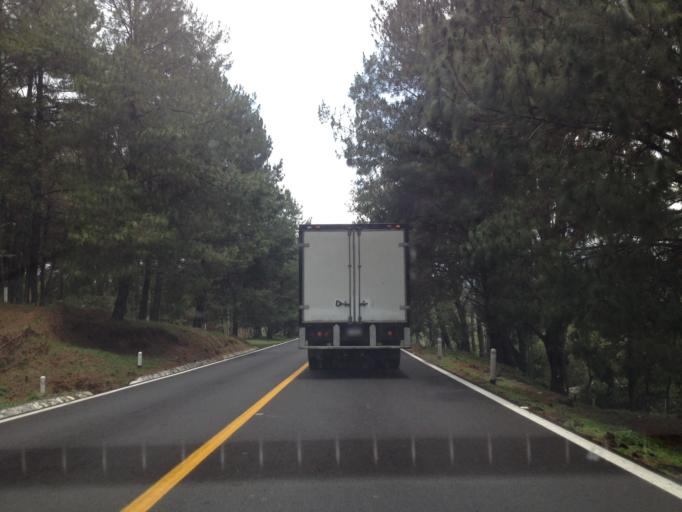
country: MX
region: Michoacan
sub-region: Patzcuaro
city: Santa Maria Huiramangaro (San Juan Tumbio)
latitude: 19.5005
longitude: -101.7551
